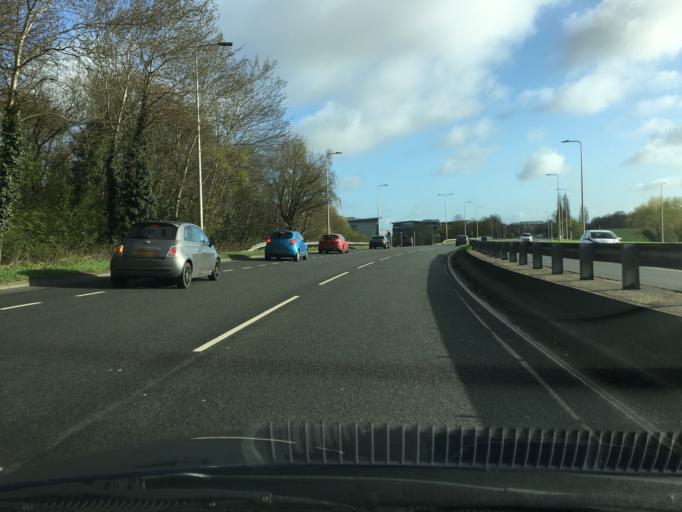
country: GB
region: England
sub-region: Bracknell Forest
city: Bracknell
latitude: 51.4061
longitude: -0.7693
